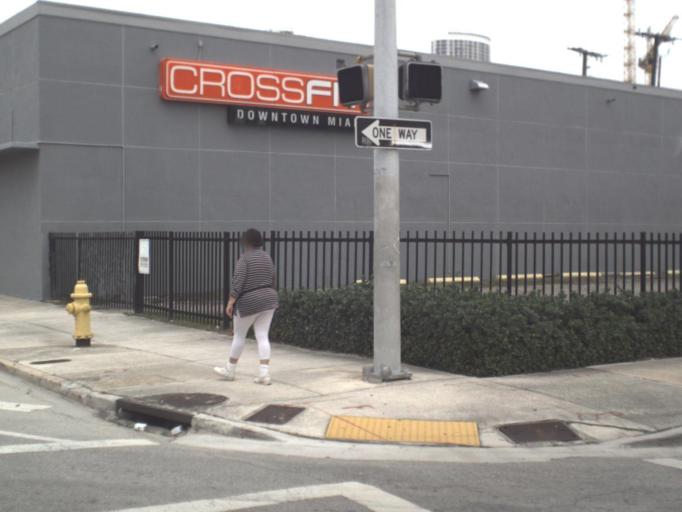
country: US
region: Florida
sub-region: Miami-Dade County
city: Miami
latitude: 25.7869
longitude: -80.1923
